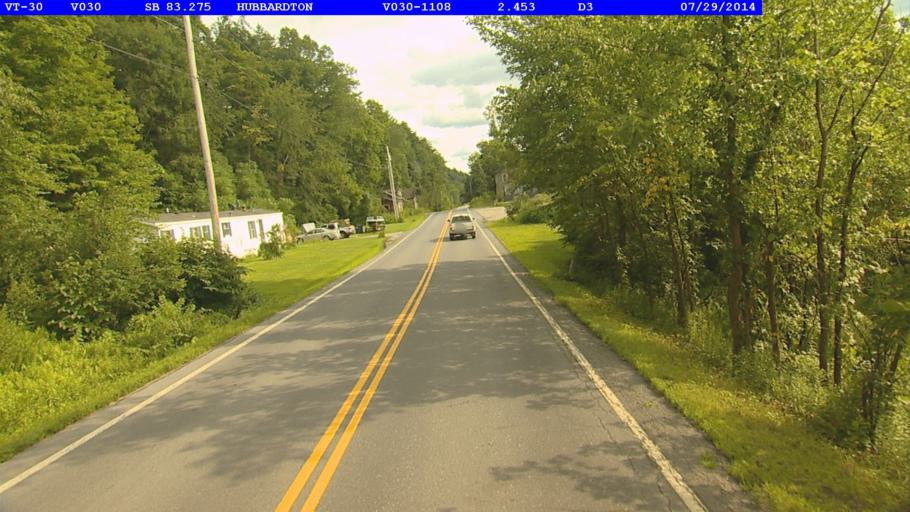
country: US
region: Vermont
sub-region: Rutland County
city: Castleton
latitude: 43.7133
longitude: -73.1849
